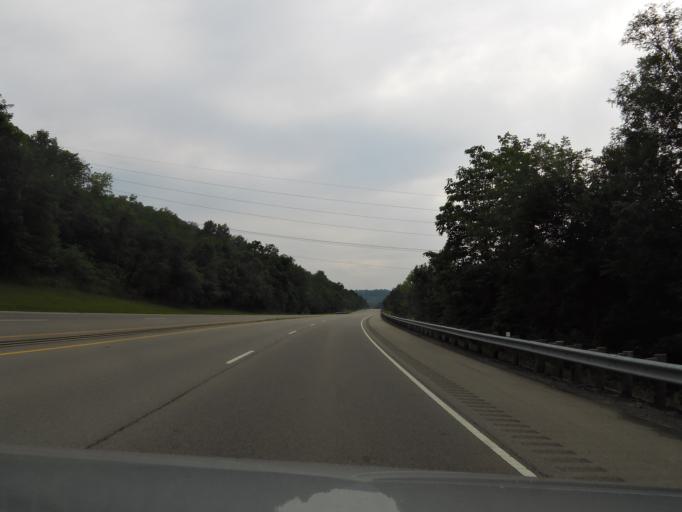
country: US
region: Ohio
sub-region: Brown County
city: Ripley
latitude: 38.7496
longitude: -83.8277
